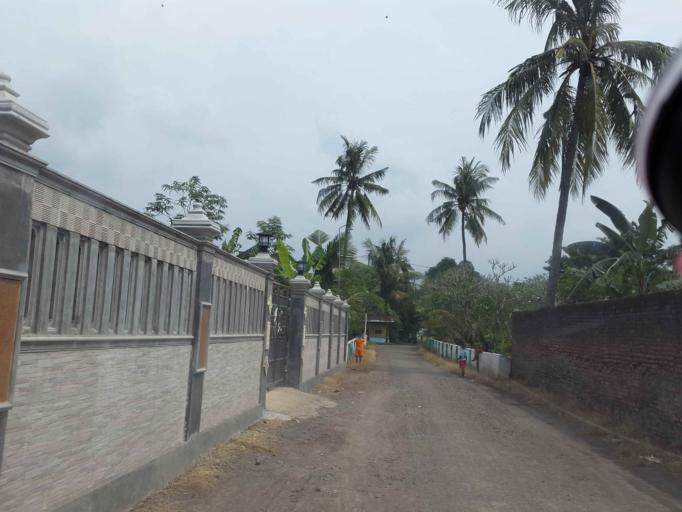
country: ID
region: Central Java
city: Pemalang
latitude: -6.8759
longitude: 109.2998
